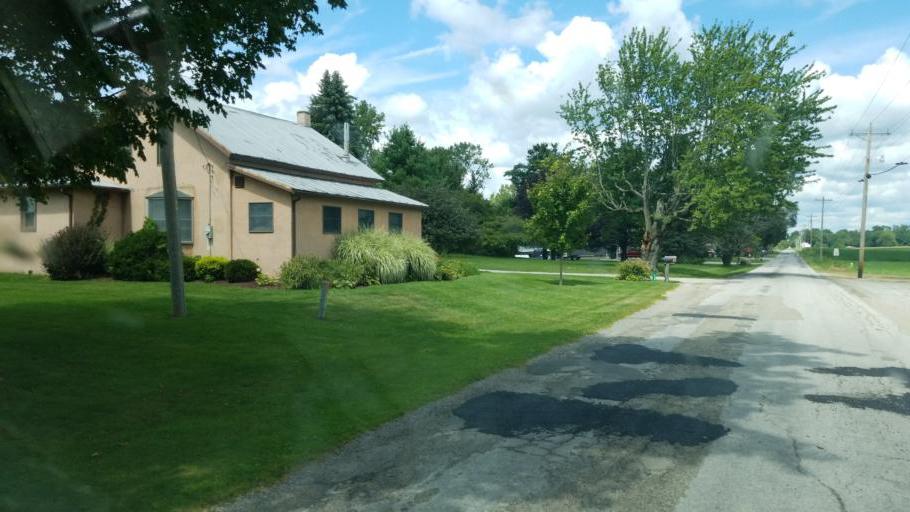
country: US
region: Ohio
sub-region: Knox County
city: Centerburg
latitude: 40.3644
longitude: -82.7246
